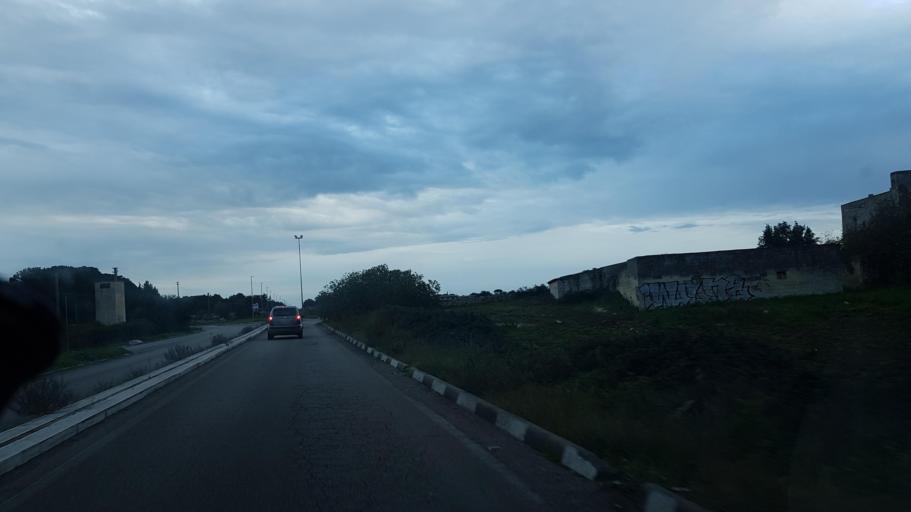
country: IT
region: Apulia
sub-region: Provincia di Lecce
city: Merine
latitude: 40.3442
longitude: 18.2053
